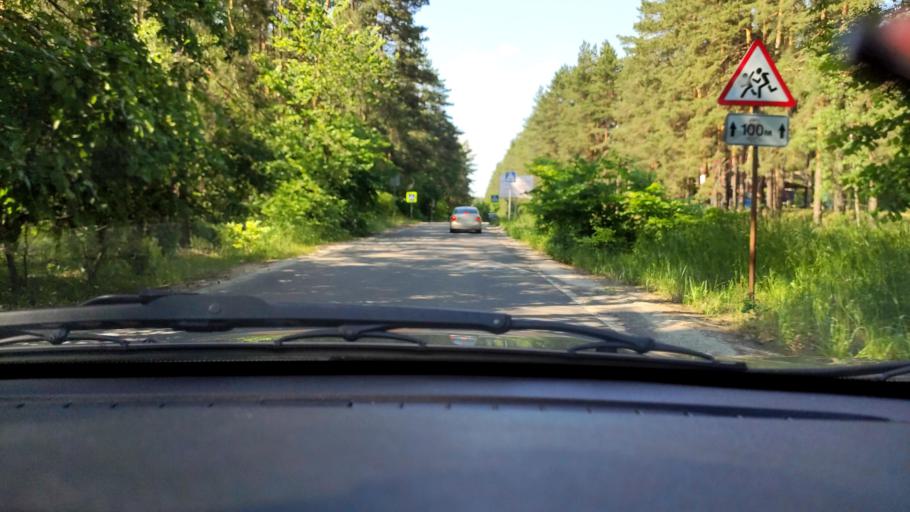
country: RU
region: Voronezj
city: Somovo
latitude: 51.7630
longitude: 39.3656
